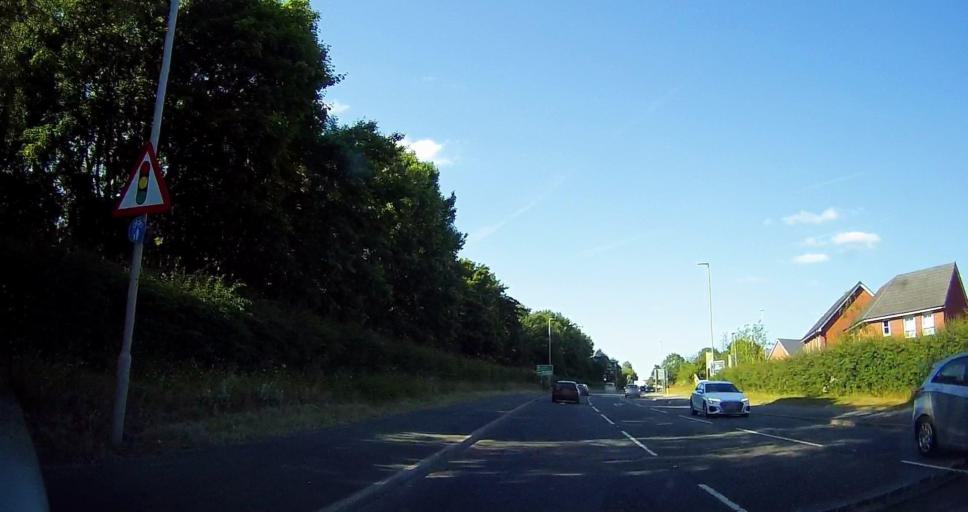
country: GB
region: England
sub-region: Cheshire East
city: Sandbach
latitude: 53.1496
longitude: -2.3511
